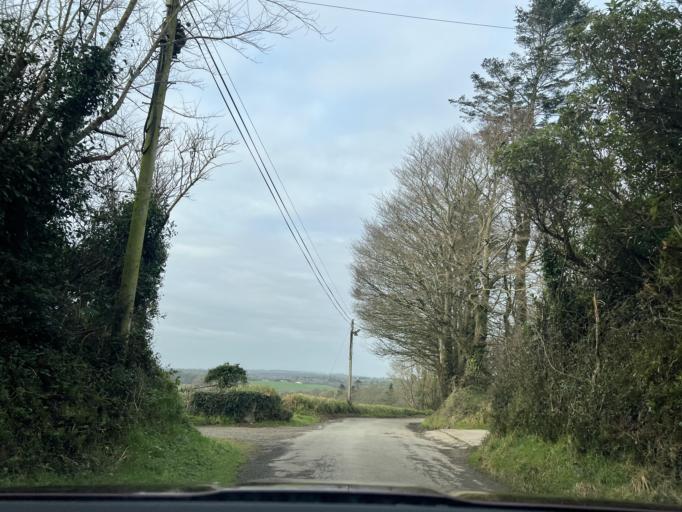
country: IE
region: Leinster
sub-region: Loch Garman
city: Castlebridge
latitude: 52.3747
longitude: -6.5412
